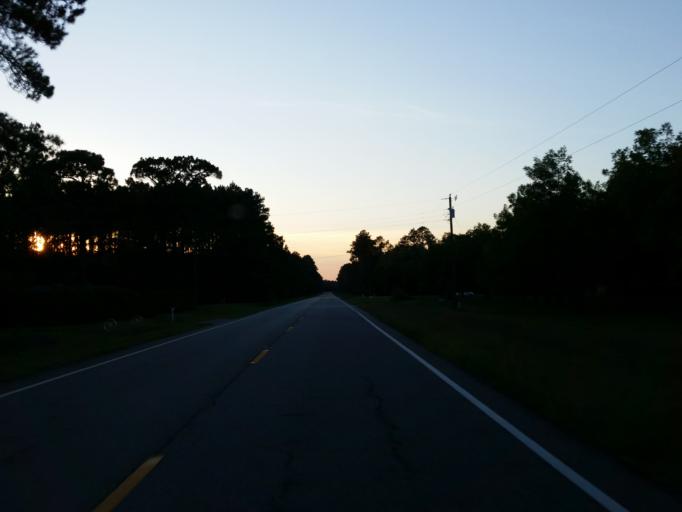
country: US
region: Georgia
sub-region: Berrien County
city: Nashville
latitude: 31.2290
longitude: -83.3015
